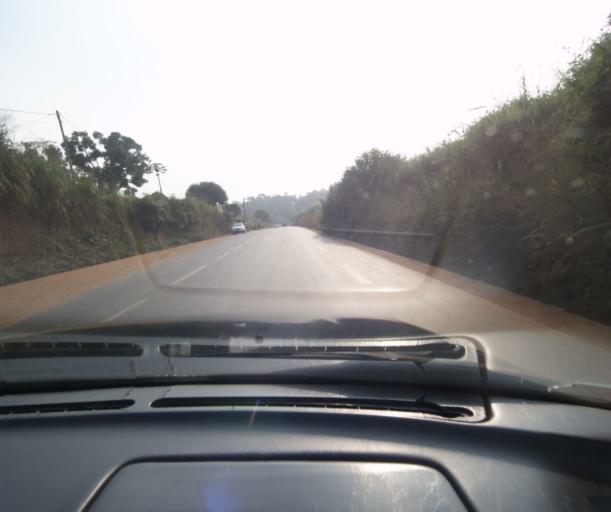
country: CM
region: Centre
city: Okoa
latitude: 3.9584
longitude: 11.5357
